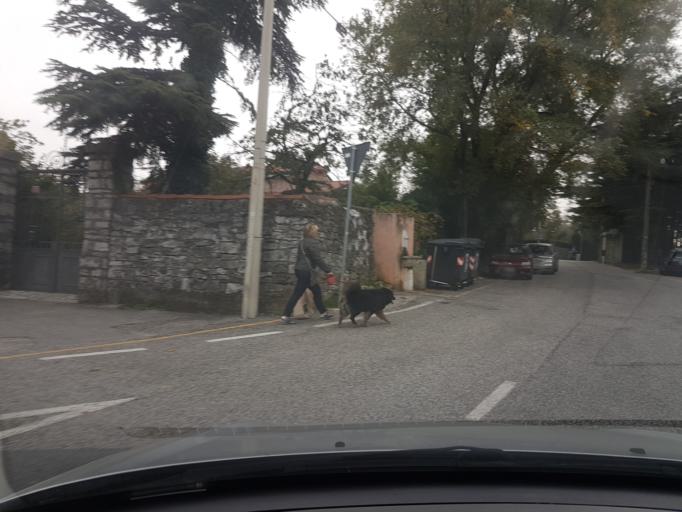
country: IT
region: Friuli Venezia Giulia
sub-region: Provincia di Trieste
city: Prosecco-Contovello
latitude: 45.7085
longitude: 13.7307
